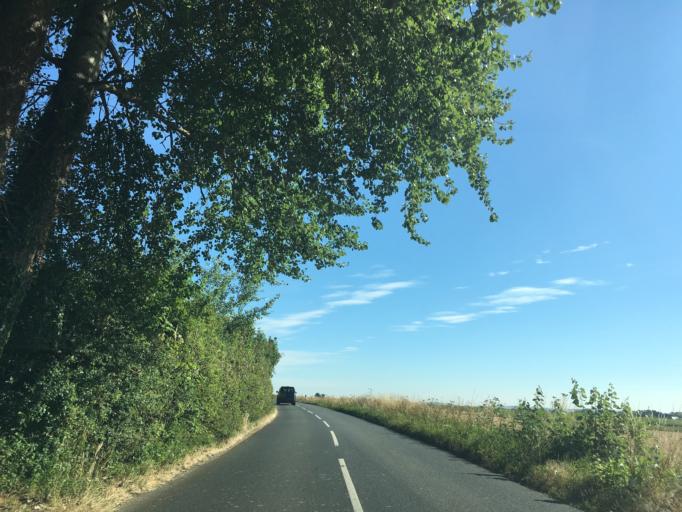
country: GB
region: England
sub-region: Isle of Wight
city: Niton
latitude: 50.6146
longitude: -1.2824
